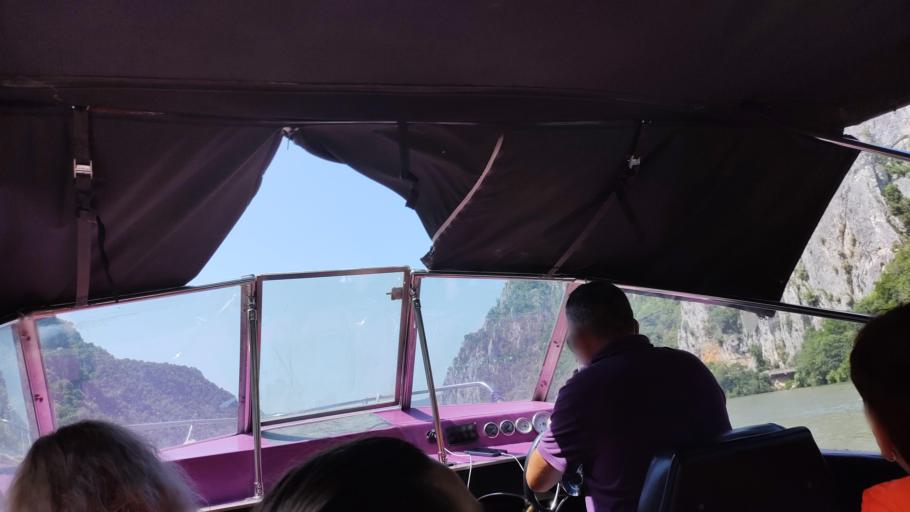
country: RO
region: Mehedinti
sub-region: Comuna Dubova
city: Dubova
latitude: 44.6364
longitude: 22.2938
